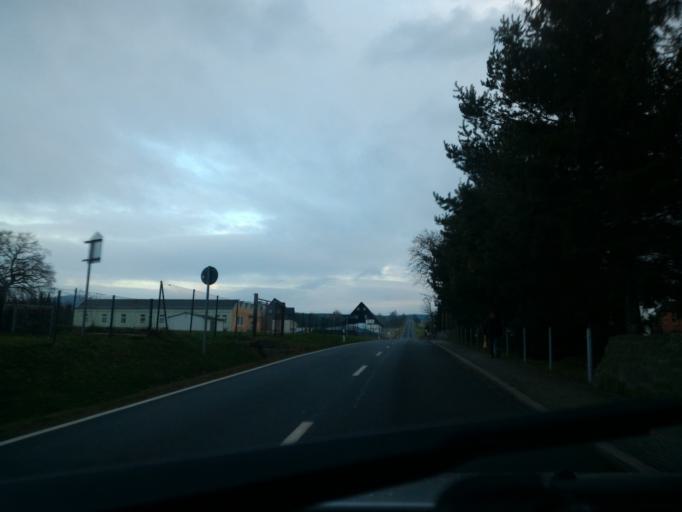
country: DE
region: Saxony
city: Grossschonau
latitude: 50.8996
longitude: 14.6585
